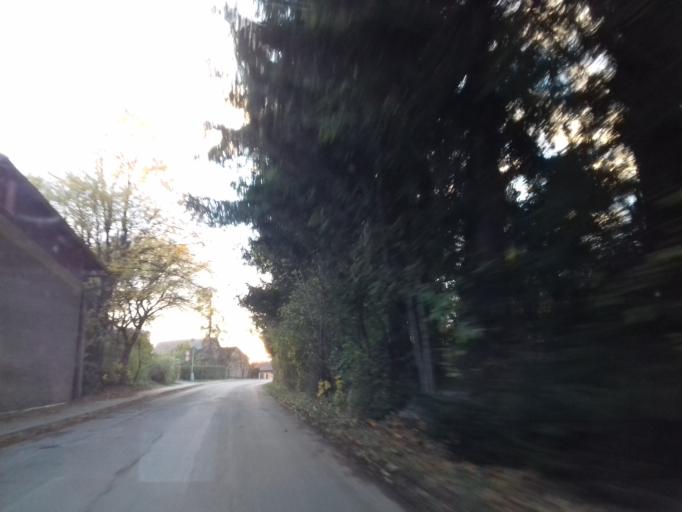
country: CZ
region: Pardubicky
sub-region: Okres Chrudim
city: Skutec
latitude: 49.7981
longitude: 15.9637
